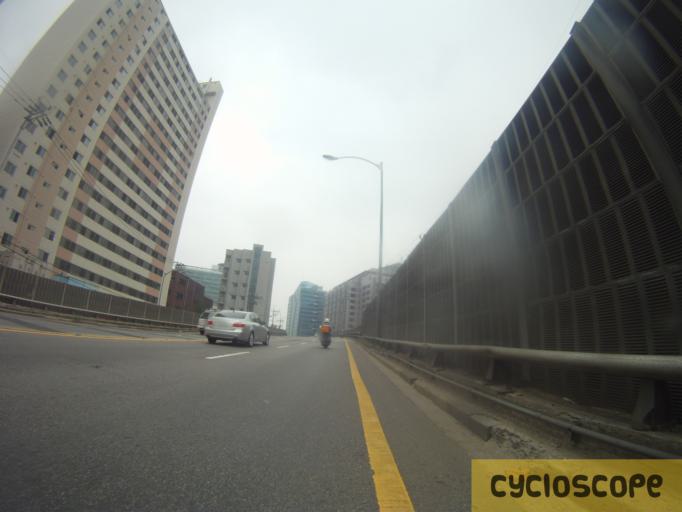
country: KR
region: Gyeonggi-do
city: Kwangmyong
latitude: 37.4665
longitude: 126.8895
